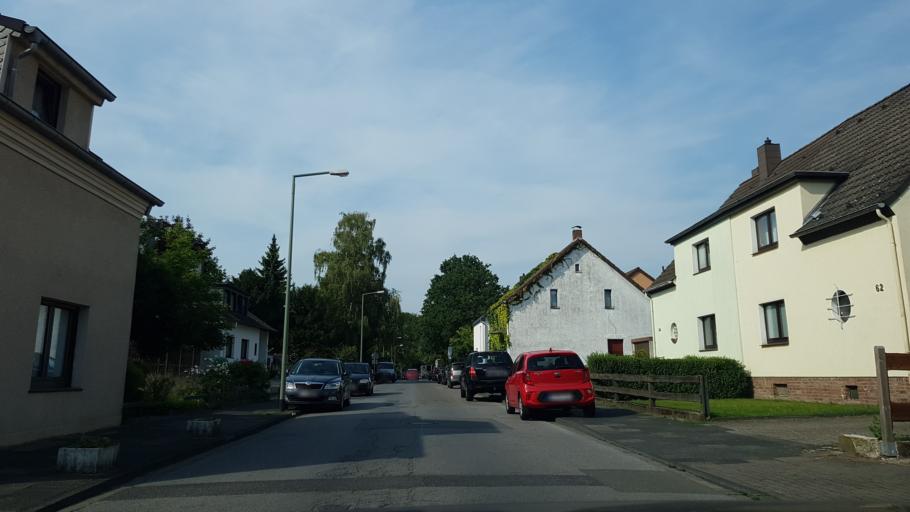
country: DE
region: North Rhine-Westphalia
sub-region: Regierungsbezirk Dusseldorf
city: Hochfeld
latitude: 51.3878
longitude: 6.7675
